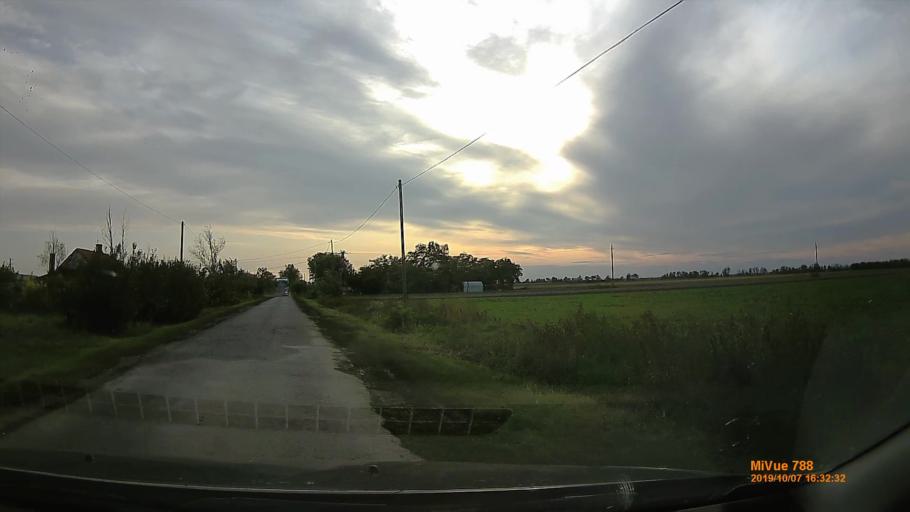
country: HU
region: Bekes
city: Szarvas
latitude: 46.7992
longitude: 20.6324
